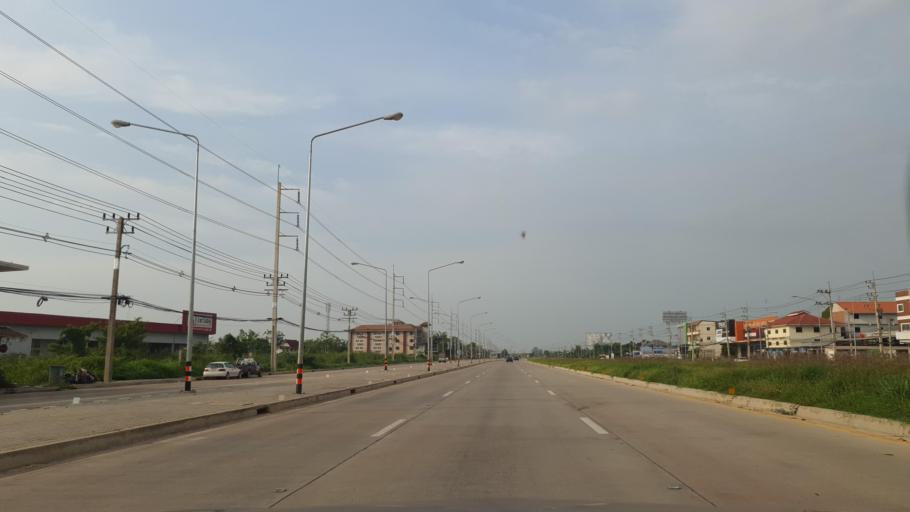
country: TH
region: Phitsanulok
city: Phitsanulok
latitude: 16.8161
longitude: 100.3312
